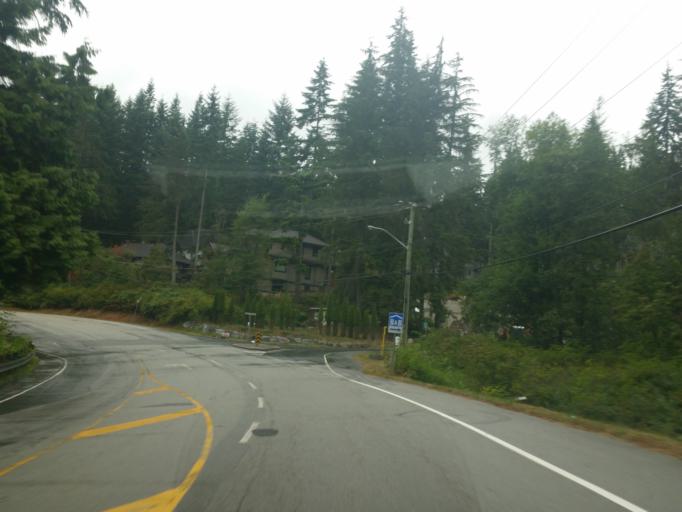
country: CA
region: British Columbia
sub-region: Greater Vancouver Regional District
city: Anmore
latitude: 49.3137
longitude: -122.8761
